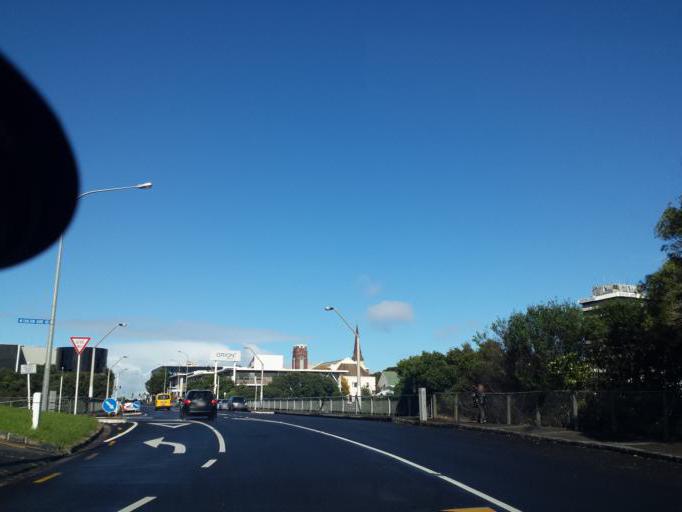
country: NZ
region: Auckland
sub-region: Auckland
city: Auckland
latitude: -36.8624
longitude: 174.7650
